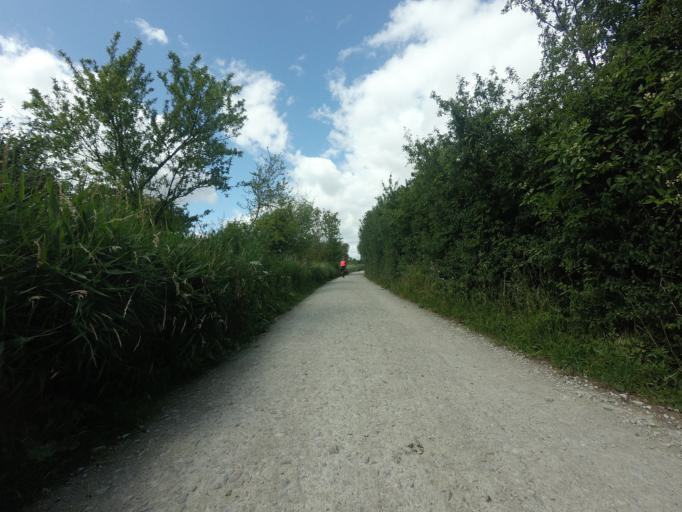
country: GB
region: England
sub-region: Kent
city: Gravesend
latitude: 51.4371
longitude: 0.4350
